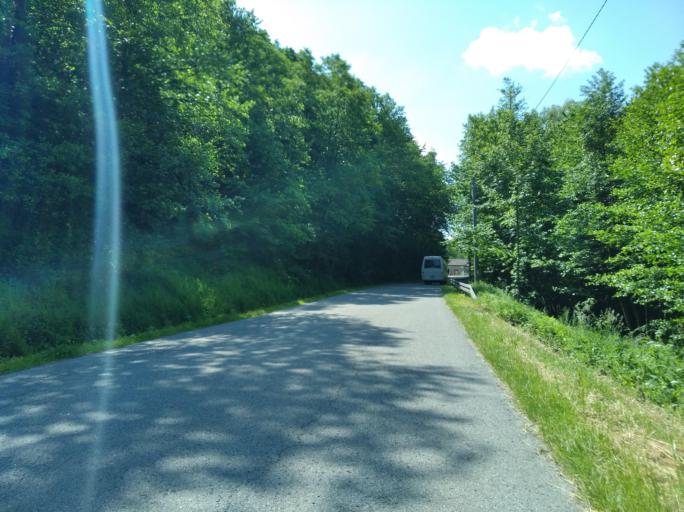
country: PL
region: Subcarpathian Voivodeship
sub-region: Powiat ropczycko-sedziszowski
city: Zagorzyce
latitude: 49.9879
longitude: 21.6455
